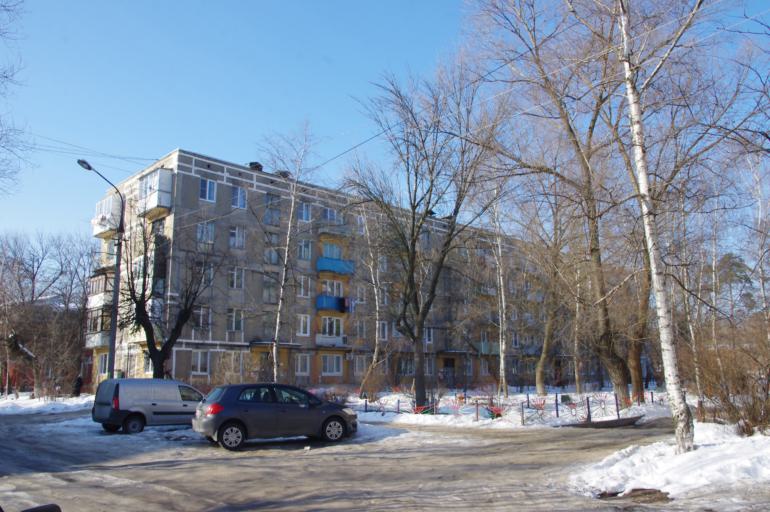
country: RU
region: Moskovskaya
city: Noginsk
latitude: 55.8786
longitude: 38.4735
